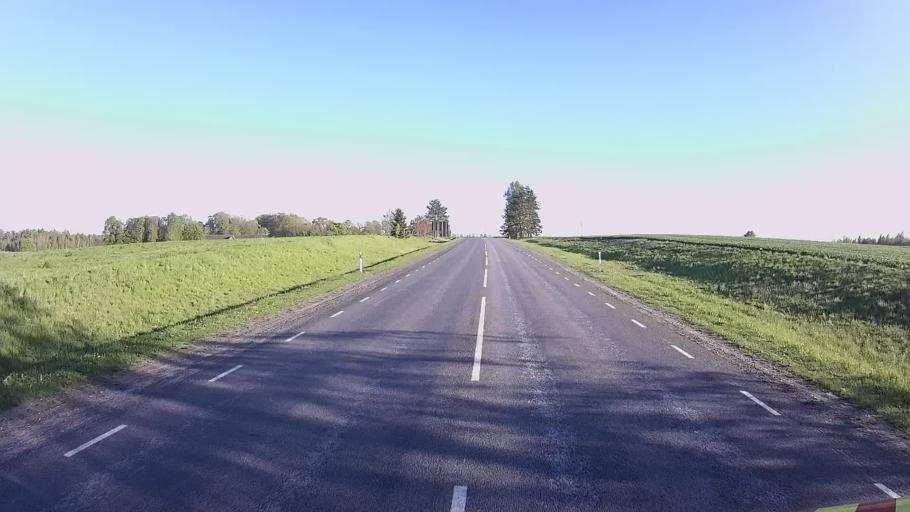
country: EE
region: Viljandimaa
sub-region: Viljandi linn
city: Viljandi
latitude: 58.4005
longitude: 25.5917
